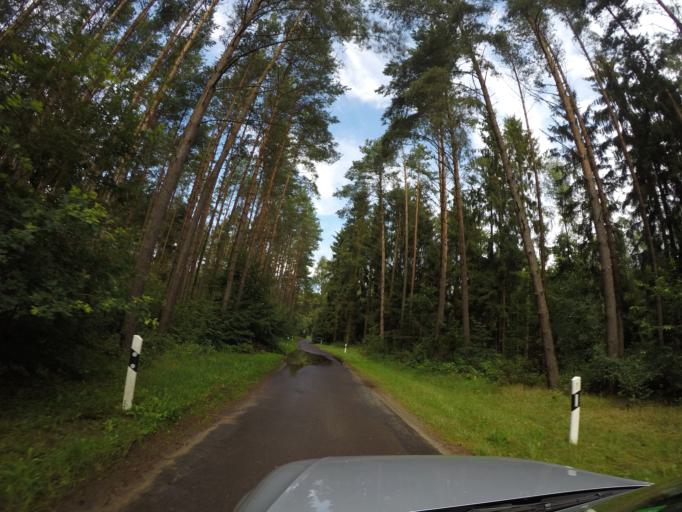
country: DE
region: Mecklenburg-Vorpommern
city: Wesenberg
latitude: 53.3196
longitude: 12.8631
